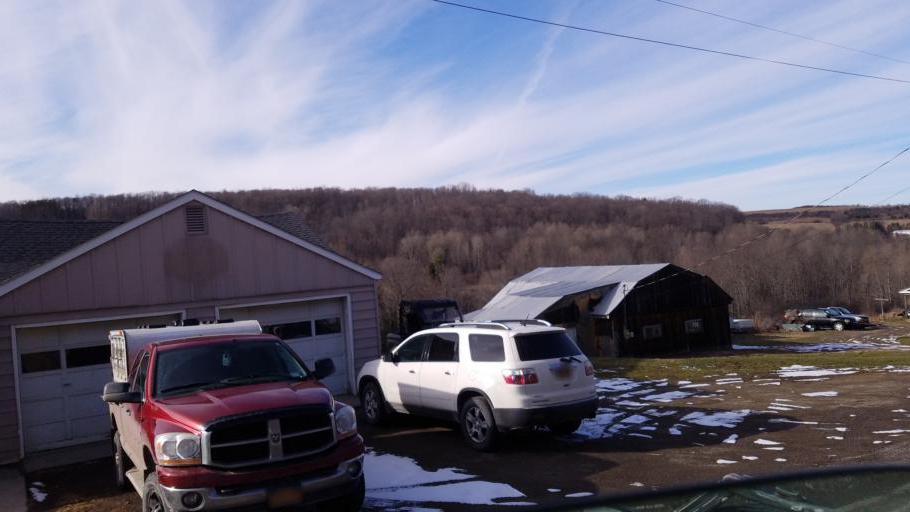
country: US
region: New York
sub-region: Allegany County
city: Wellsville
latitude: 42.0956
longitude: -77.9783
